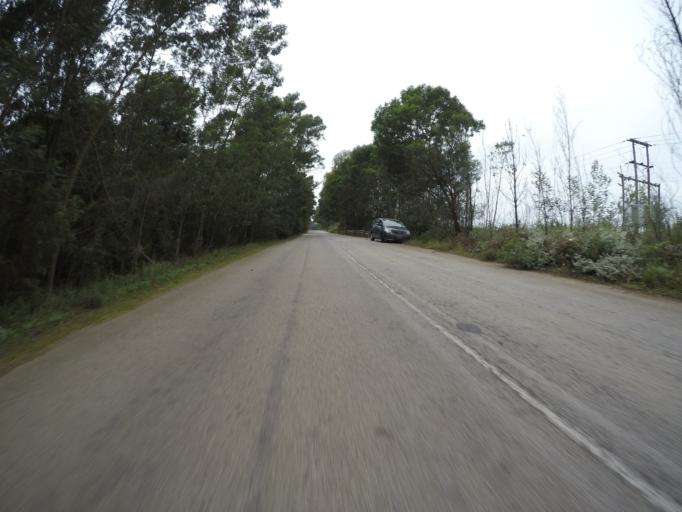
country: ZA
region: Eastern Cape
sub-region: Cacadu District Municipality
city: Kareedouw
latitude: -33.9980
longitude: 24.1694
